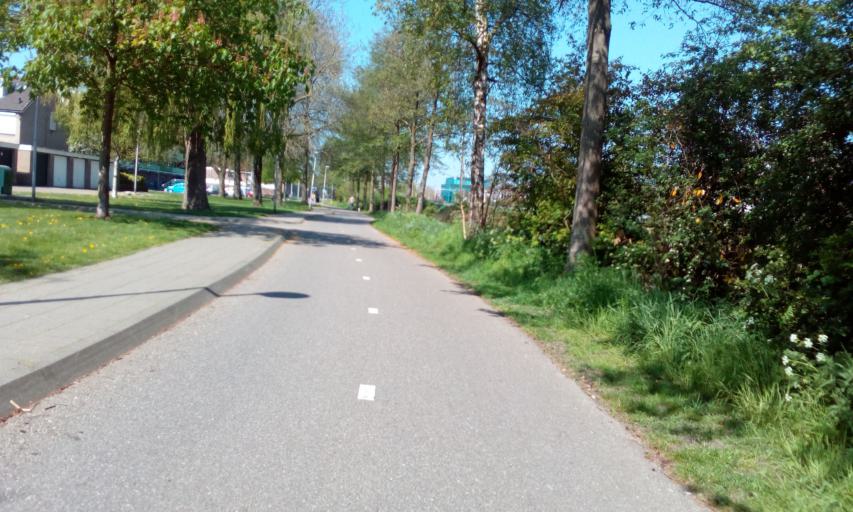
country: NL
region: South Holland
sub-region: Bodegraven-Reeuwijk
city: Bodegraven
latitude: 52.0802
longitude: 4.7520
